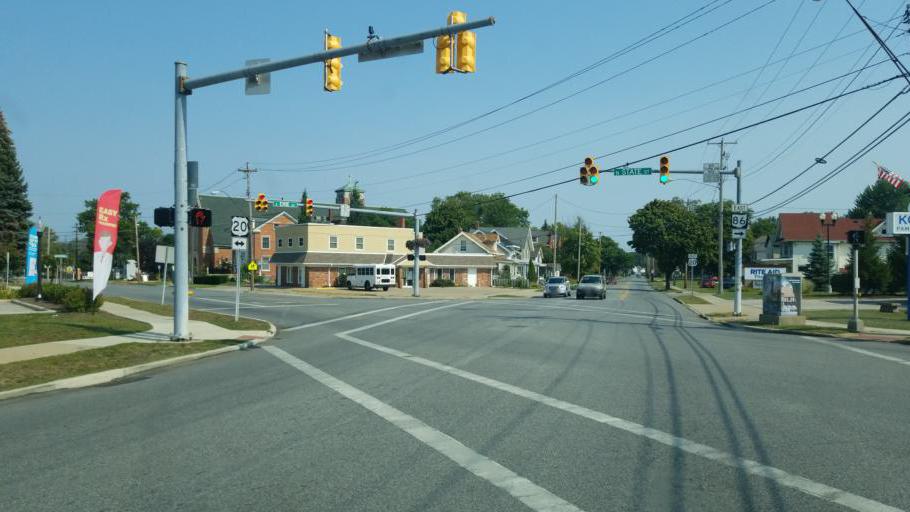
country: US
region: Ohio
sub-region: Lake County
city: Painesville
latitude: 41.7291
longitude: -81.2435
